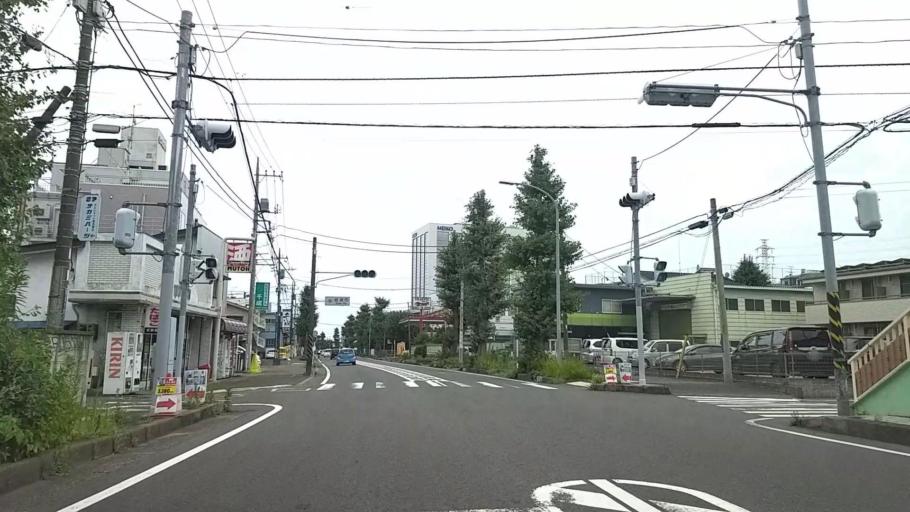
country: JP
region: Kanagawa
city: Minami-rinkan
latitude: 35.4671
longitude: 139.4299
